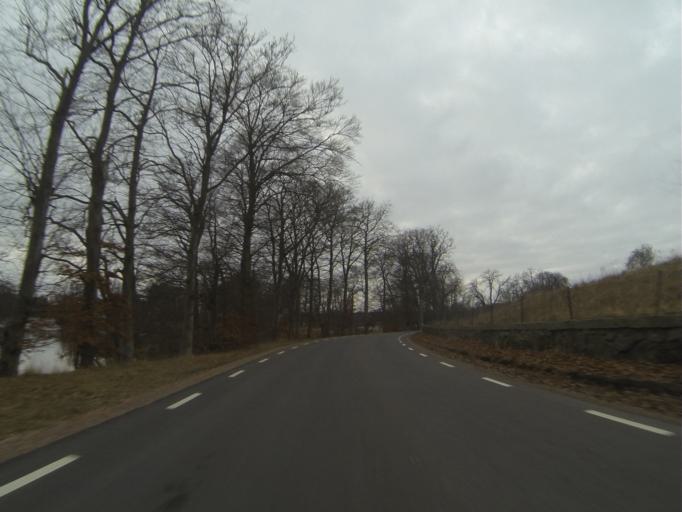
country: SE
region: Skane
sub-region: Lunds Kommun
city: Genarp
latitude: 55.5800
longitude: 13.4320
